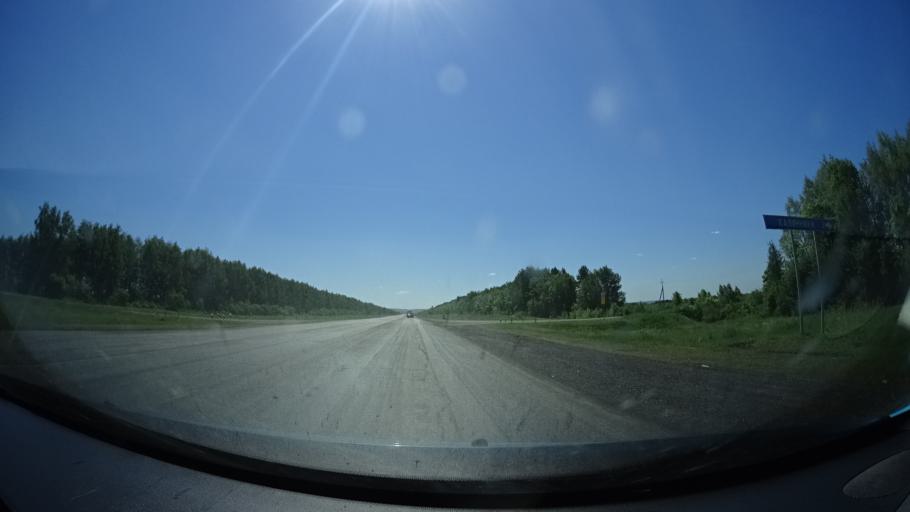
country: RU
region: Bashkortostan
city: Birsk
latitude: 55.2411
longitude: 55.7686
